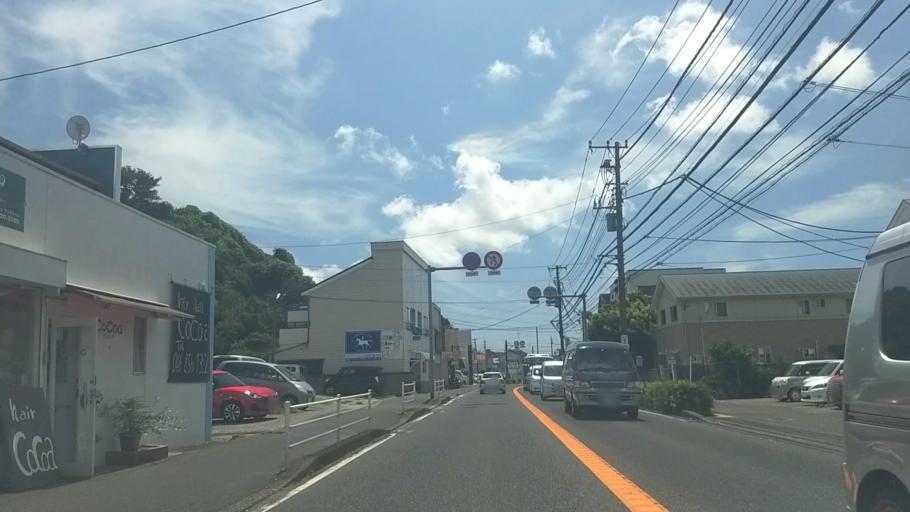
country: JP
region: Kanagawa
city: Yokosuka
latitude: 35.2219
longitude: 139.6426
